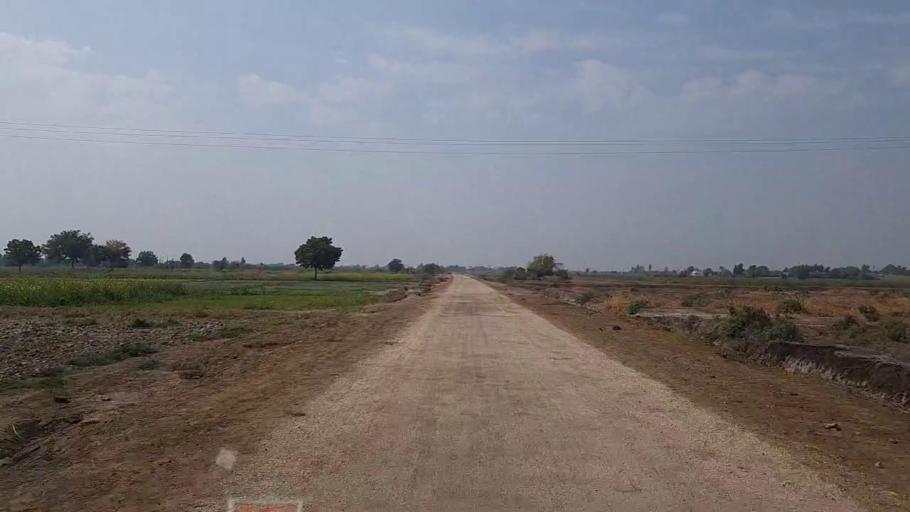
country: PK
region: Sindh
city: Mirwah Gorchani
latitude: 25.3485
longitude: 69.0810
